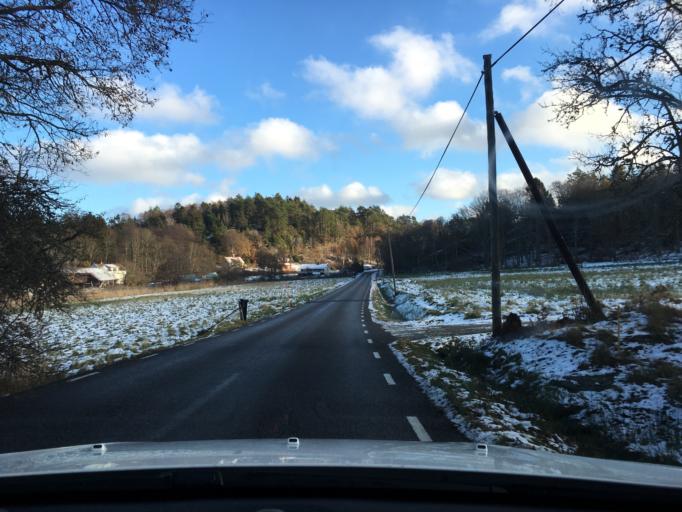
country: SE
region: Vaestra Goetaland
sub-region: Tjorns Kommun
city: Myggenas
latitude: 58.0595
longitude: 11.6870
